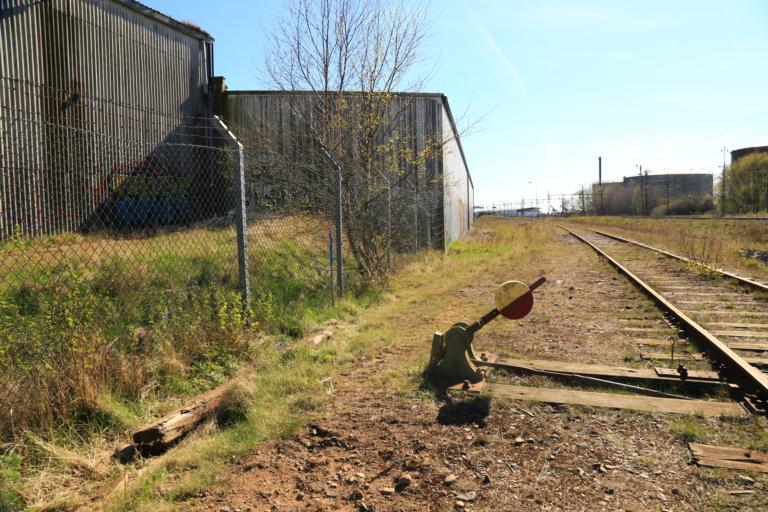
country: SE
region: Halland
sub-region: Varbergs Kommun
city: Varberg
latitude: 57.1186
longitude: 12.2535
